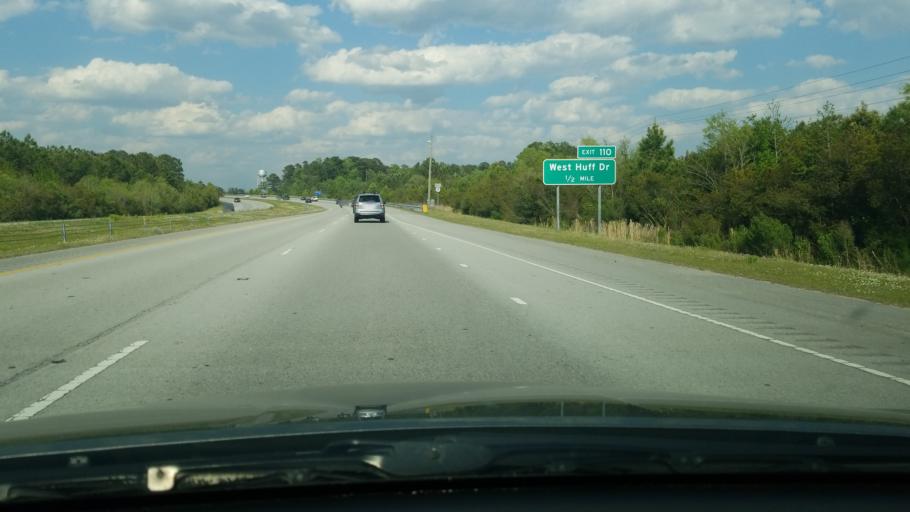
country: US
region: North Carolina
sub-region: Onslow County
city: Jacksonville
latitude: 34.7514
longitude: -77.4001
